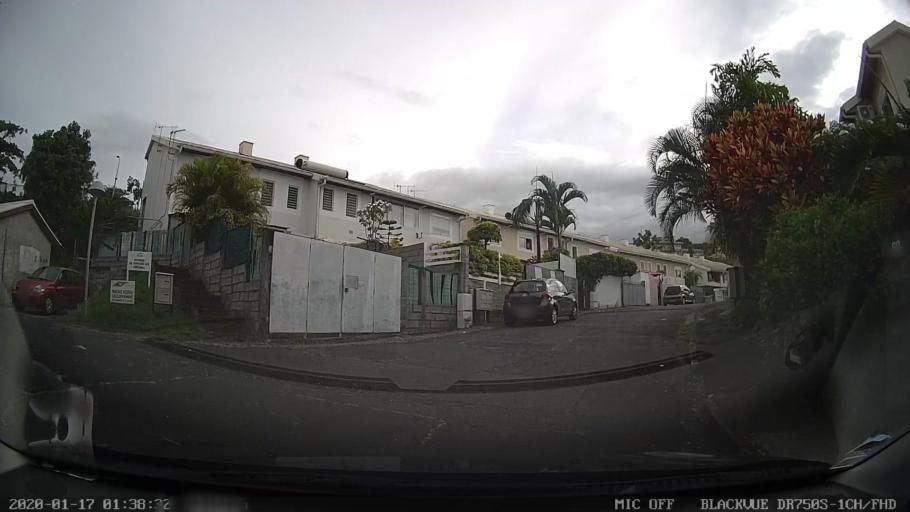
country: RE
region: Reunion
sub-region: Reunion
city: Saint-Denis
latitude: -20.9052
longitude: 55.4865
